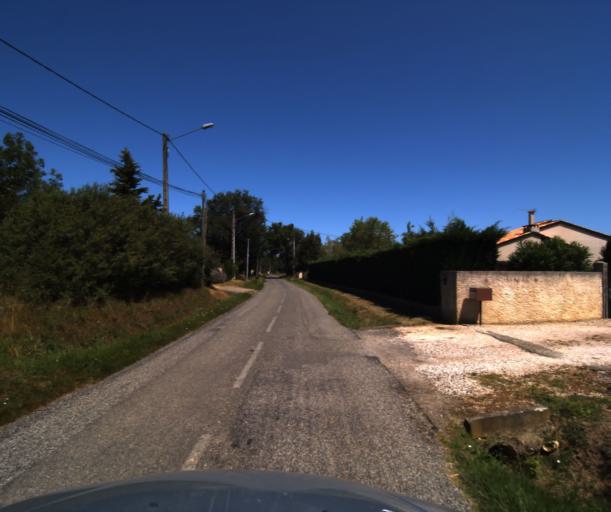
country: FR
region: Midi-Pyrenees
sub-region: Departement de la Haute-Garonne
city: Muret
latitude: 43.4546
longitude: 1.3524
